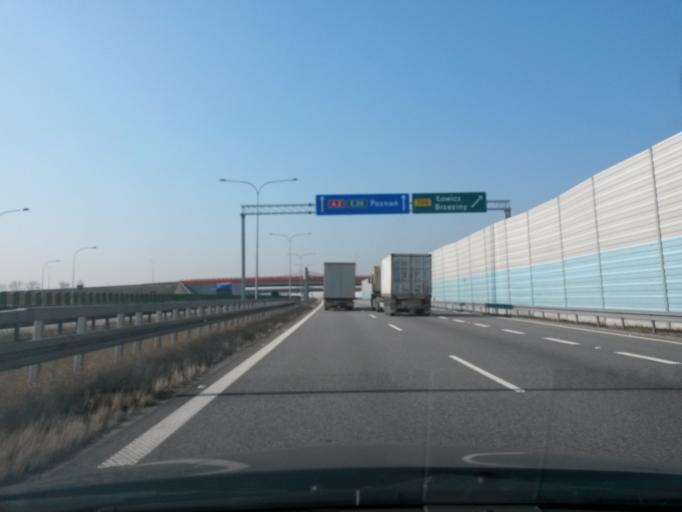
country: PL
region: Lodz Voivodeship
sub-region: powiat Lowicki
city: Lyszkowice
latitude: 51.9896
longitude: 19.8996
